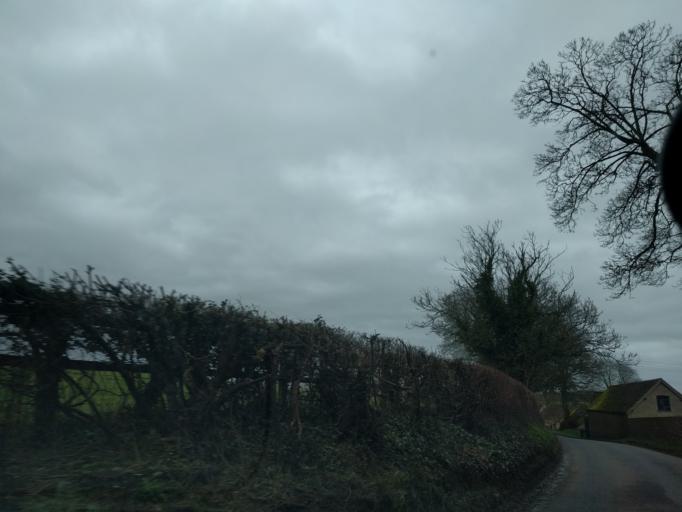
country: GB
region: England
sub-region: Gloucestershire
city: Nailsworth
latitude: 51.6327
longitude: -2.2341
